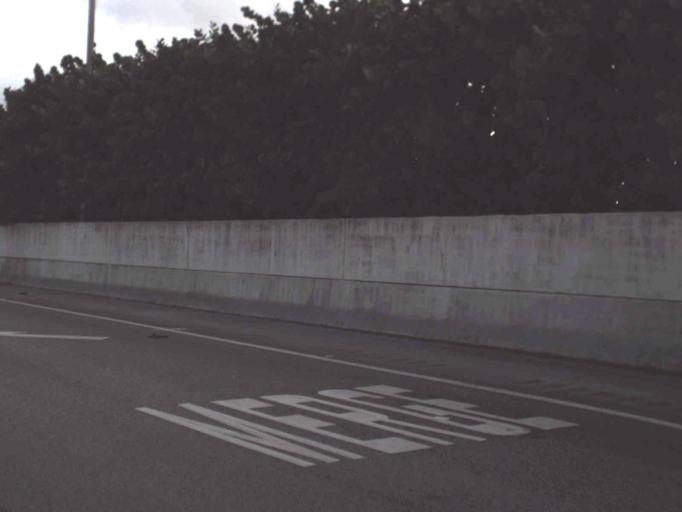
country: US
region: Florida
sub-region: Miami-Dade County
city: Scott Lake
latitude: 25.9475
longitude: -80.2272
